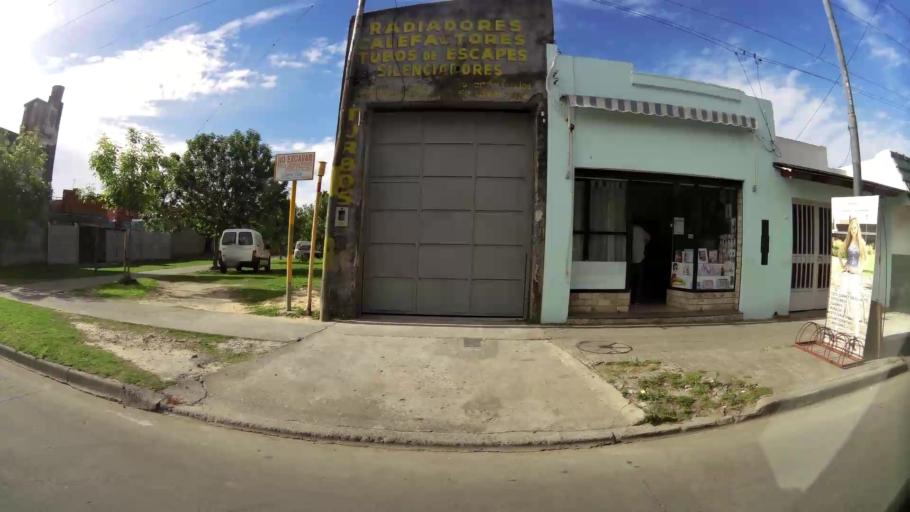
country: AR
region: Santa Fe
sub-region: Departamento de Rosario
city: Rosario
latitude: -32.9269
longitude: -60.6895
